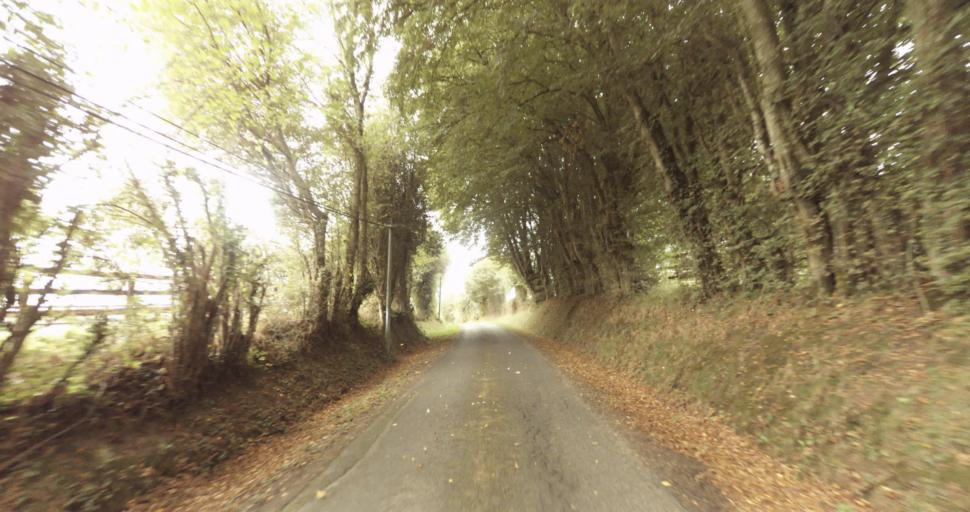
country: FR
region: Lower Normandy
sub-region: Departement de l'Orne
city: Gace
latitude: 48.7301
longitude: 0.2929
